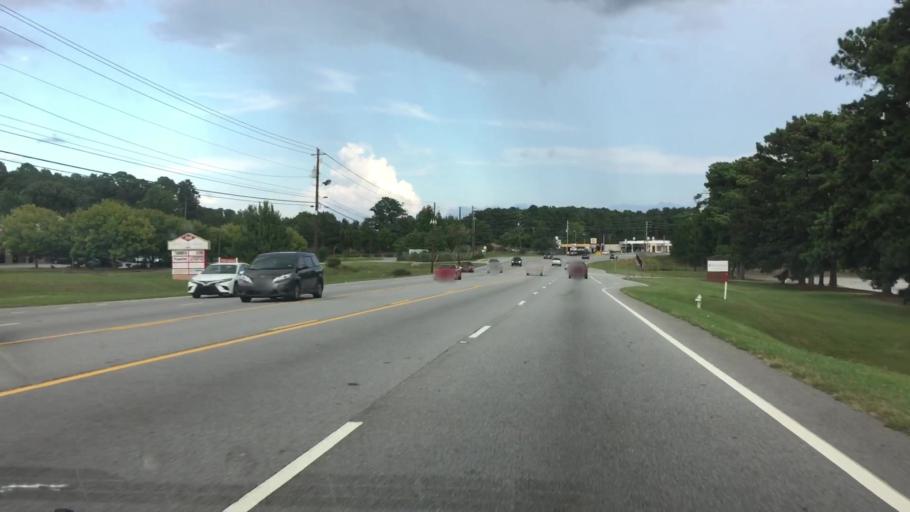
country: US
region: Georgia
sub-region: Clayton County
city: Riverdale
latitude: 33.5467
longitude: -84.4078
